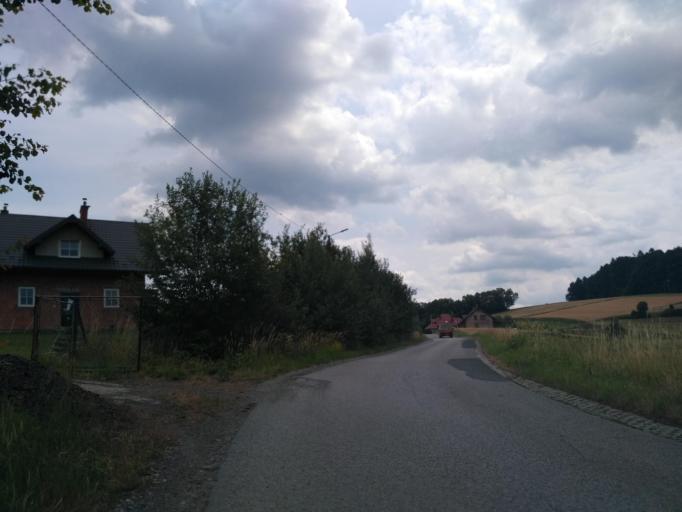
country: PL
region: Subcarpathian Voivodeship
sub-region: Powiat ropczycko-sedziszowski
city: Niedzwiada
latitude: 50.0358
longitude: 21.5043
